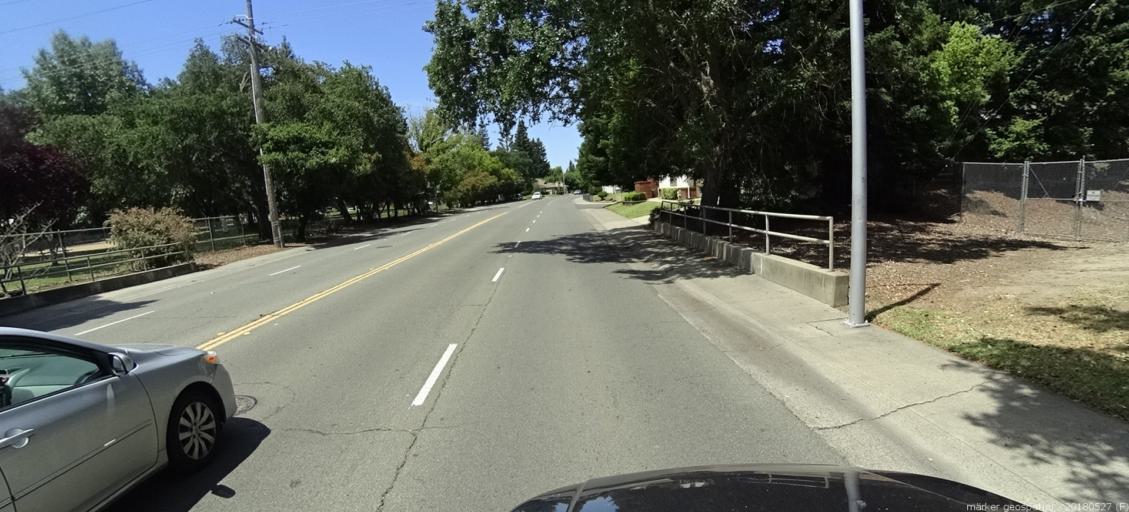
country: US
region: California
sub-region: Yolo County
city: West Sacramento
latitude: 38.5246
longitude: -121.5130
